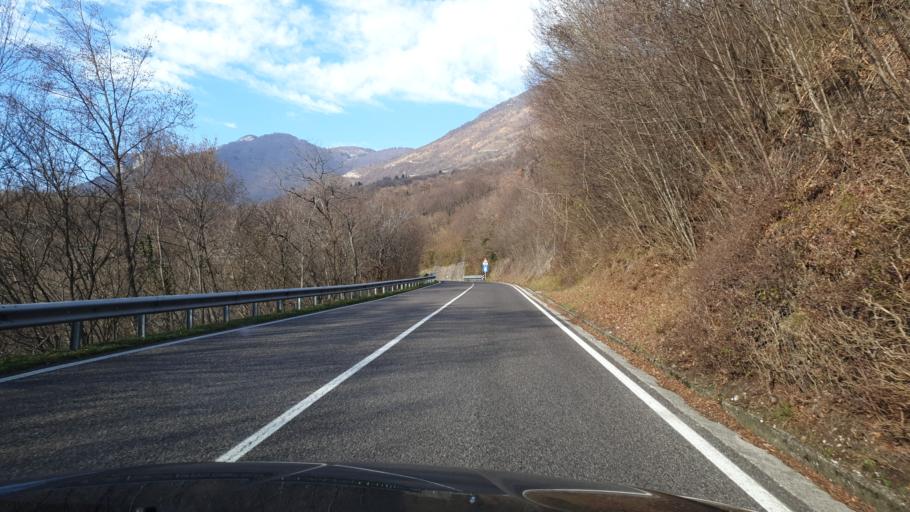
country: IT
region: Veneto
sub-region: Provincia di Vicenza
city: Cogollo del Cengio
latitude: 45.7858
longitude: 11.4396
